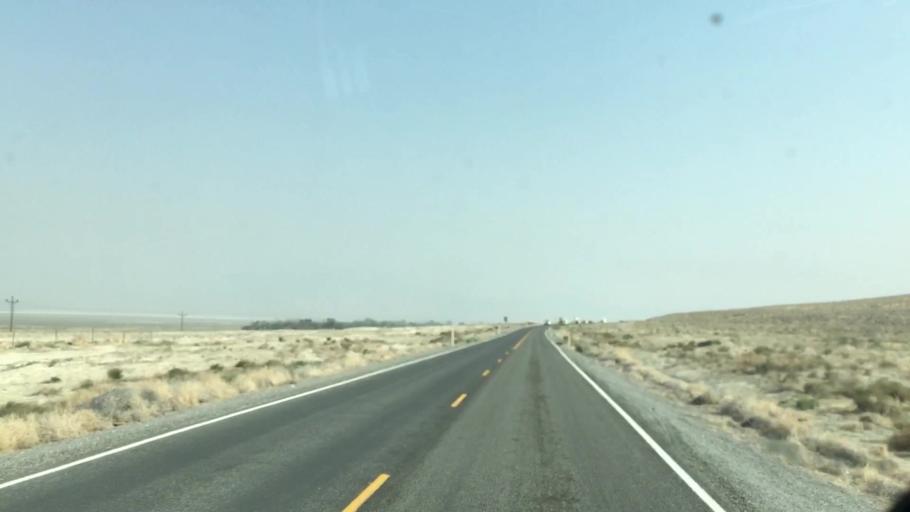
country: US
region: Nevada
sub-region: Pershing County
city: Lovelock
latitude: 40.5626
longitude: -119.3394
